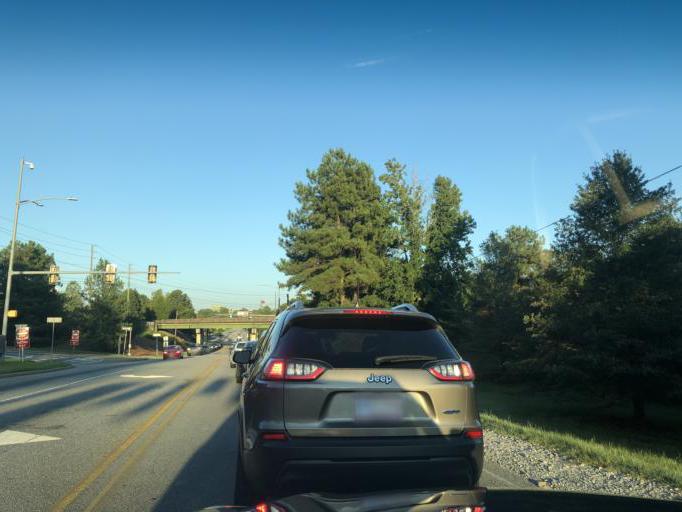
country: US
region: Georgia
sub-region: Muscogee County
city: Columbus
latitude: 32.5224
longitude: -84.8941
